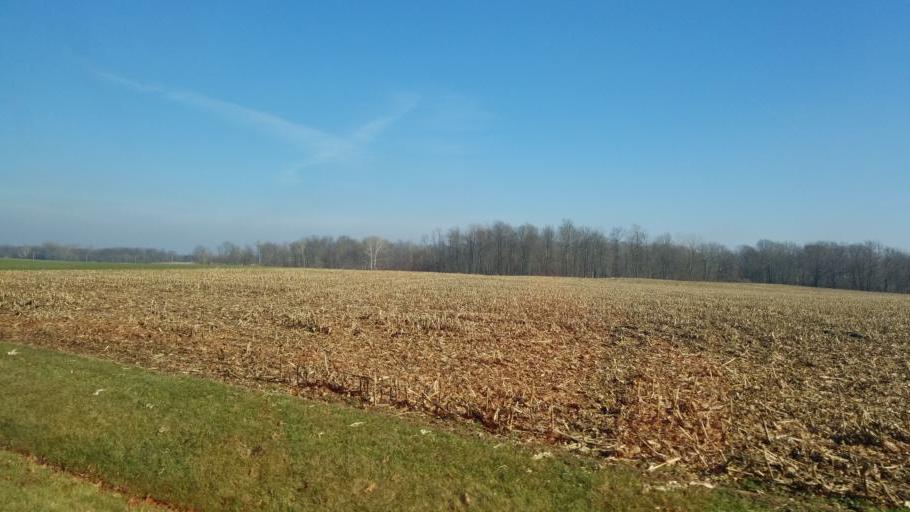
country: US
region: Ohio
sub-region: Crawford County
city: Bucyrus
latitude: 40.9424
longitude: -83.0742
